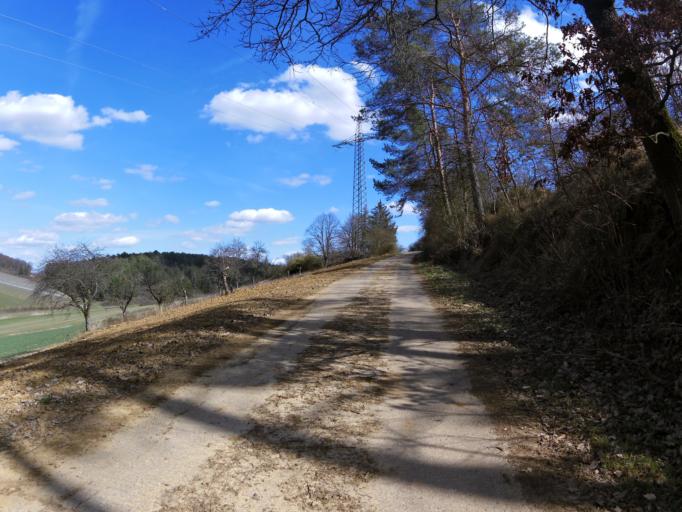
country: DE
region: Bavaria
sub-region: Regierungsbezirk Unterfranken
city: Erlabrunn
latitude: 49.8424
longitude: 9.8157
